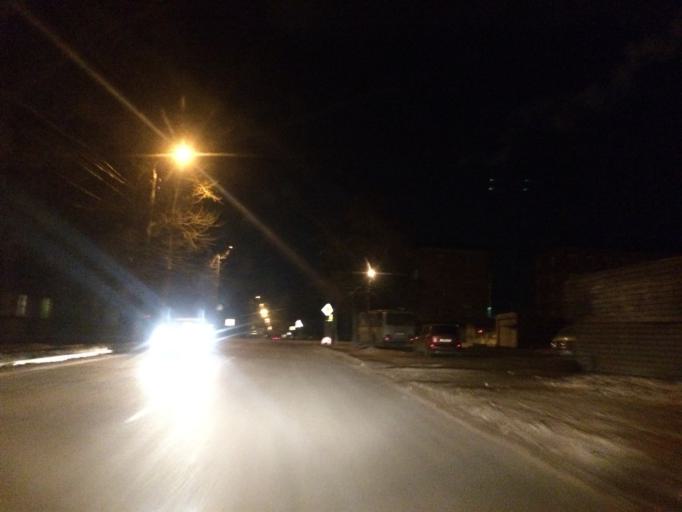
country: RU
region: Tula
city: Mendeleyevskiy
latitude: 54.1627
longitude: 37.5757
